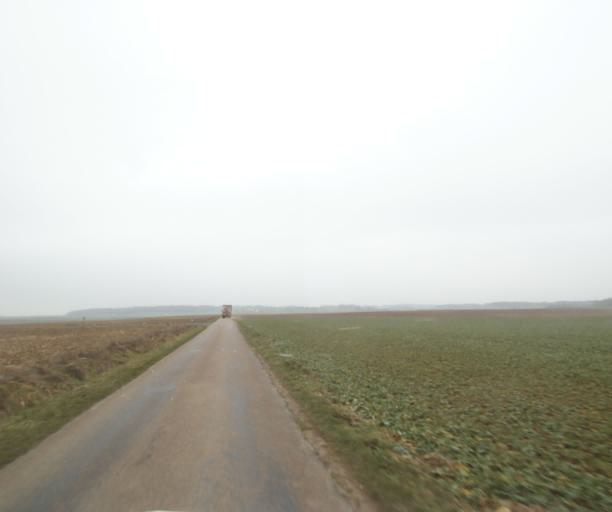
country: FR
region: Champagne-Ardenne
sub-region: Departement de la Haute-Marne
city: Chevillon
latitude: 48.5057
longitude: 5.0835
